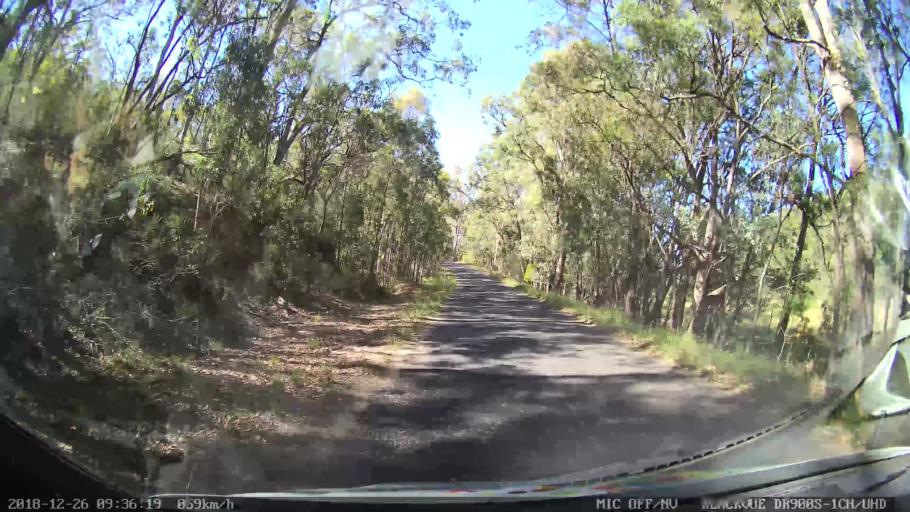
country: AU
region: New South Wales
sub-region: Mid-Western Regional
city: Kandos
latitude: -32.9228
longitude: 150.0401
